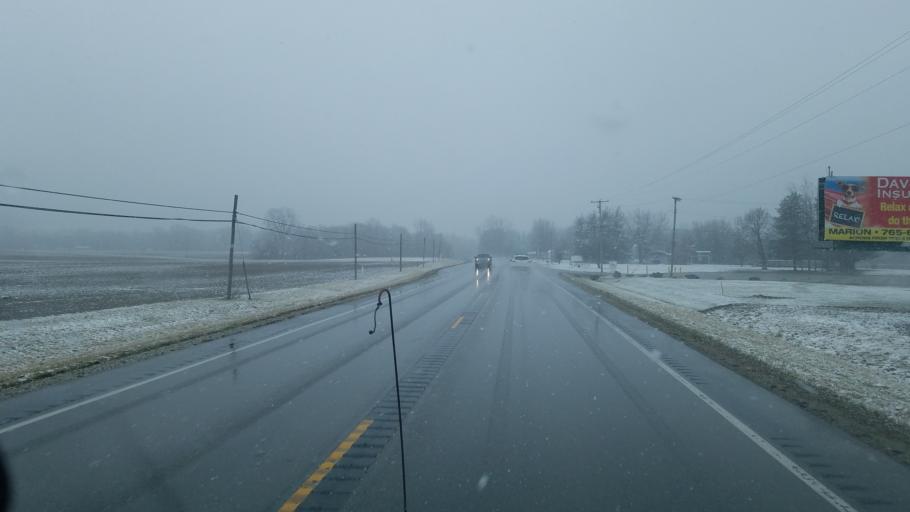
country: US
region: Indiana
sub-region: Grant County
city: Marion
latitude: 40.6201
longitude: -85.6982
